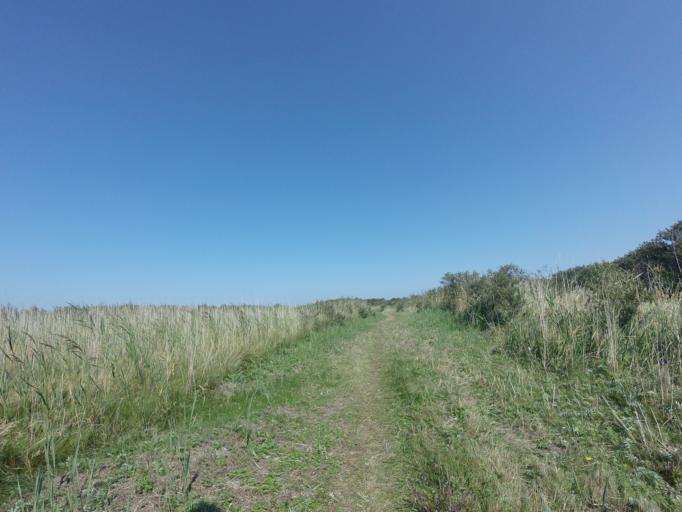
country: NL
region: Friesland
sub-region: Gemeente Schiermonnikoog
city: Schiermonnikoog
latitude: 53.4947
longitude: 6.2434
